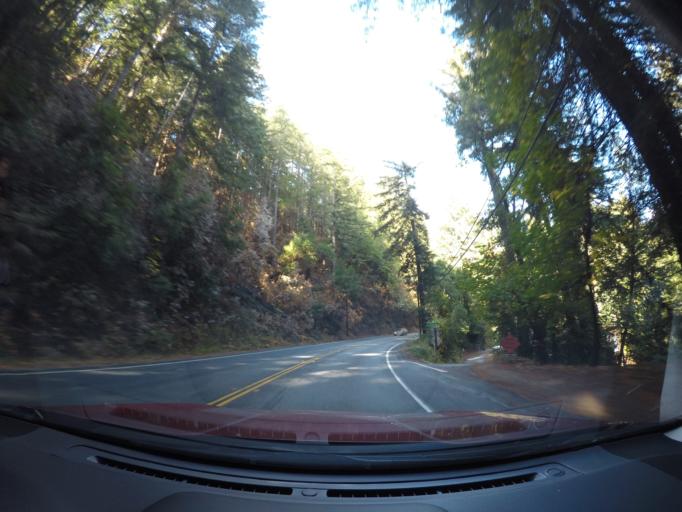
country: US
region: California
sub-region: Santa Cruz County
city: Boulder Creek
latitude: 37.1135
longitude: -122.1180
